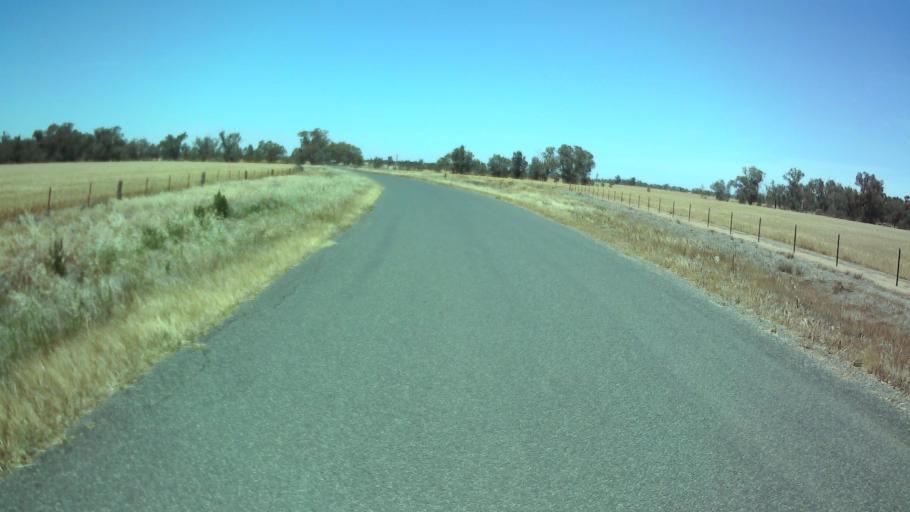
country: AU
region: New South Wales
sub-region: Weddin
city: Grenfell
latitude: -34.0356
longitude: 147.7897
